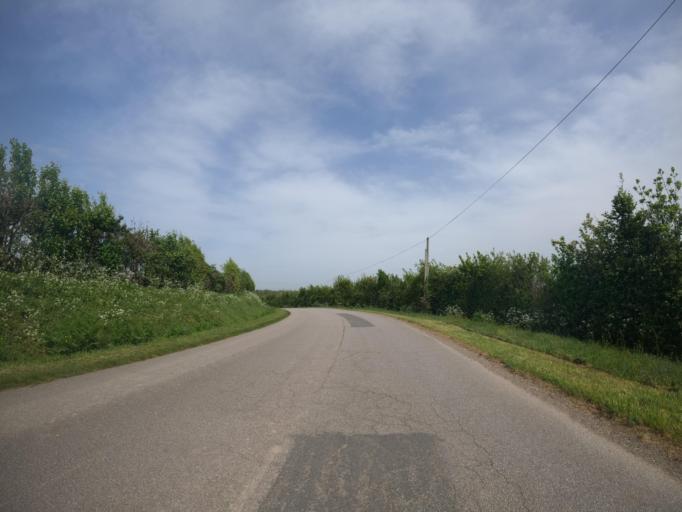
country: FR
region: Poitou-Charentes
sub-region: Departement des Deux-Sevres
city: La Chapelle-Saint-Laurent
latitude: 46.7082
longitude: -0.5057
